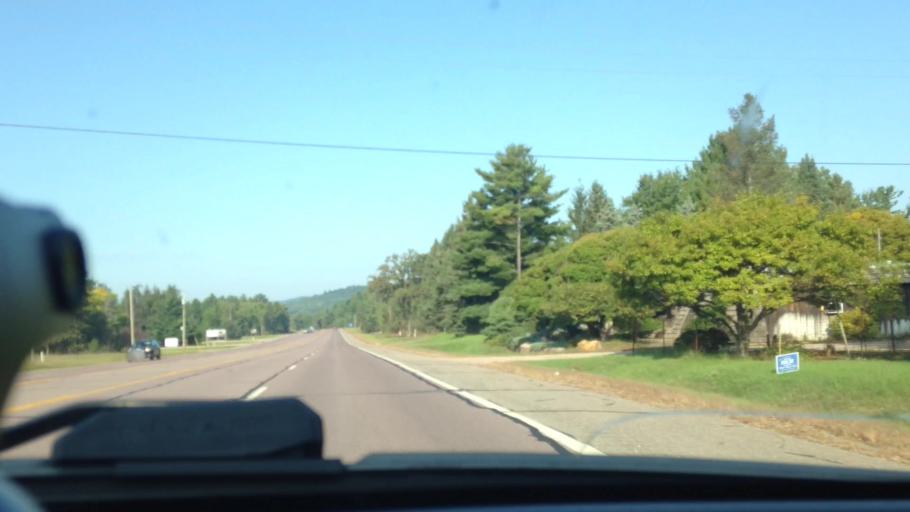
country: US
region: Michigan
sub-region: Dickinson County
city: Quinnesec
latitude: 45.8026
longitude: -87.9608
